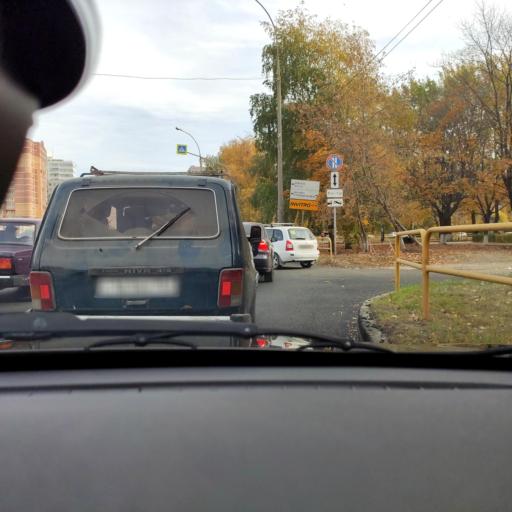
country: RU
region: Samara
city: Tol'yatti
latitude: 53.5136
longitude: 49.2919
